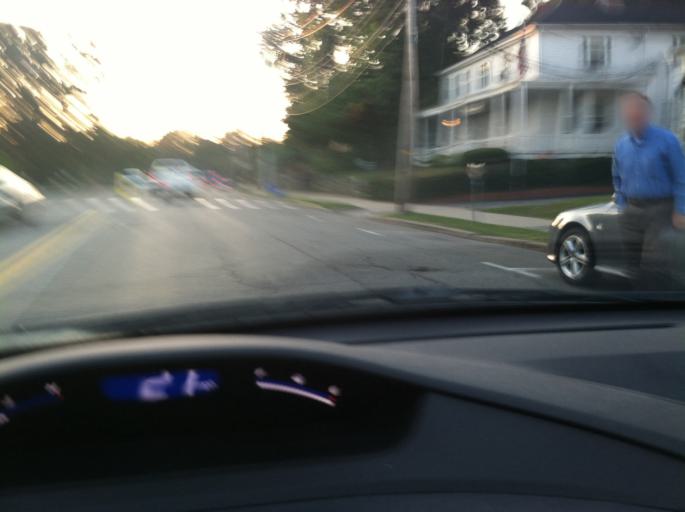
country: US
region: Massachusetts
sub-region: Middlesex County
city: Lexington
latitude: 42.4535
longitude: -71.2330
